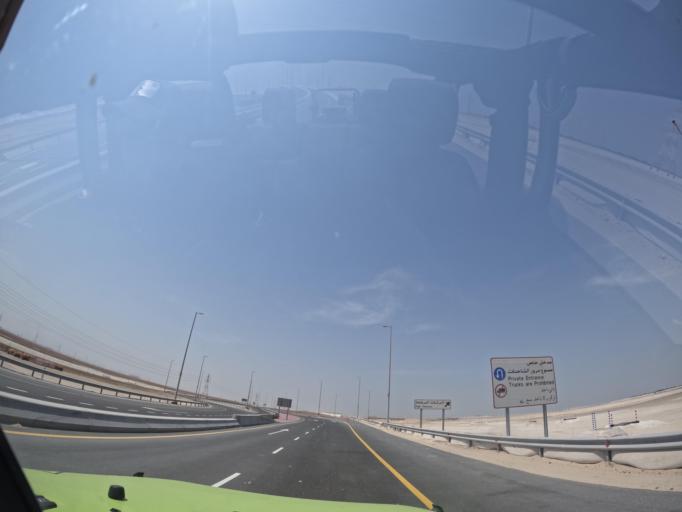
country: AE
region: Abu Dhabi
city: Abu Dhabi
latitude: 24.1655
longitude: 54.3524
